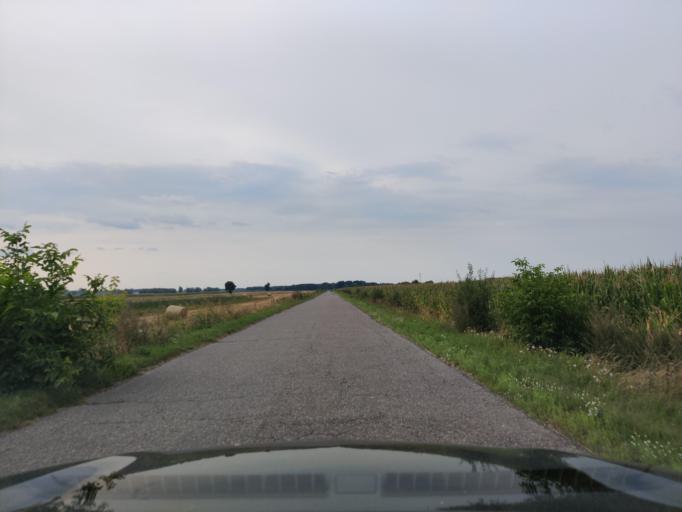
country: PL
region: Masovian Voivodeship
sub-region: Powiat pultuski
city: Obryte
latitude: 52.7190
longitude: 21.2488
